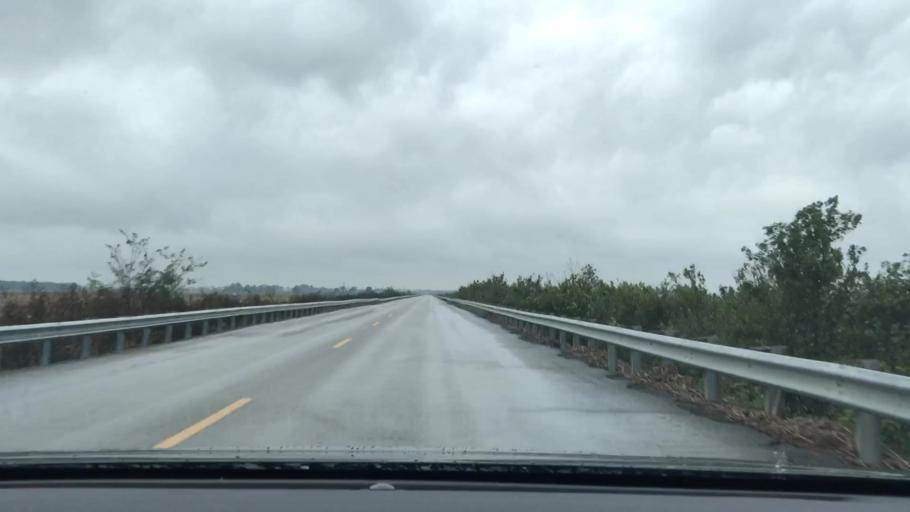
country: US
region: Kentucky
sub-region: McLean County
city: Calhoun
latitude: 37.3880
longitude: -87.3248
